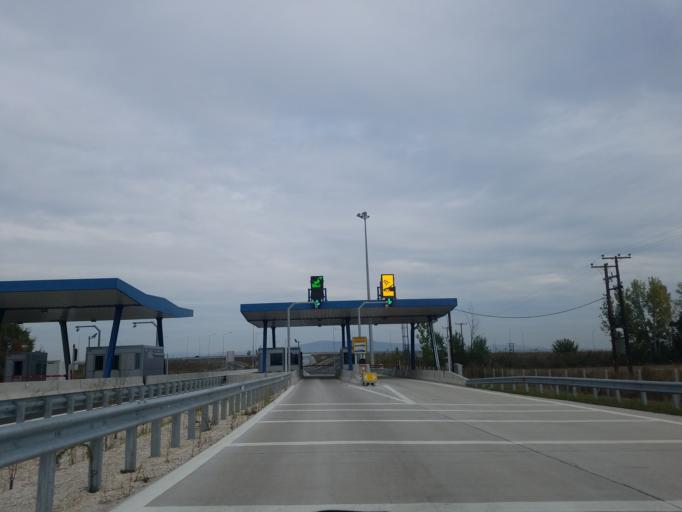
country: GR
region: Thessaly
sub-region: Nomos Kardhitsas
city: Agia Triada
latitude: 39.4742
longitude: 21.9032
